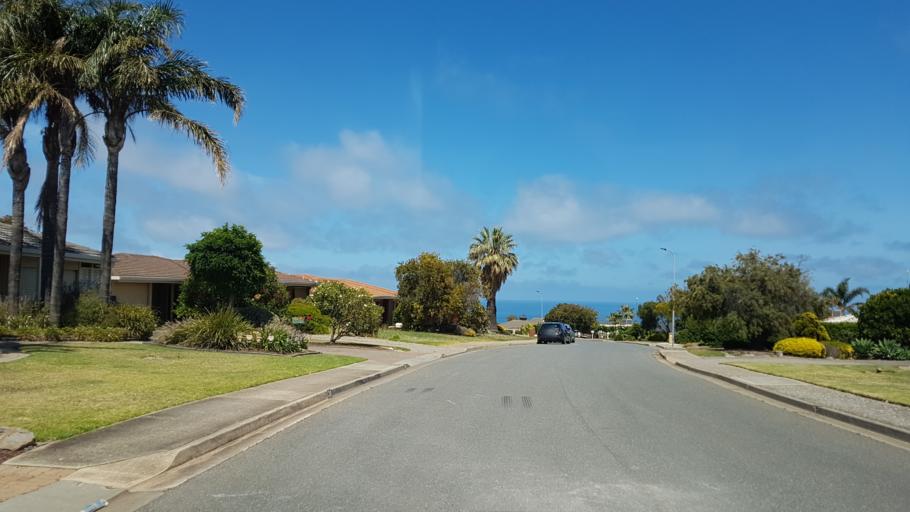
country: AU
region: South Australia
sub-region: Marion
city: Marino
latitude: -35.0649
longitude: 138.5125
